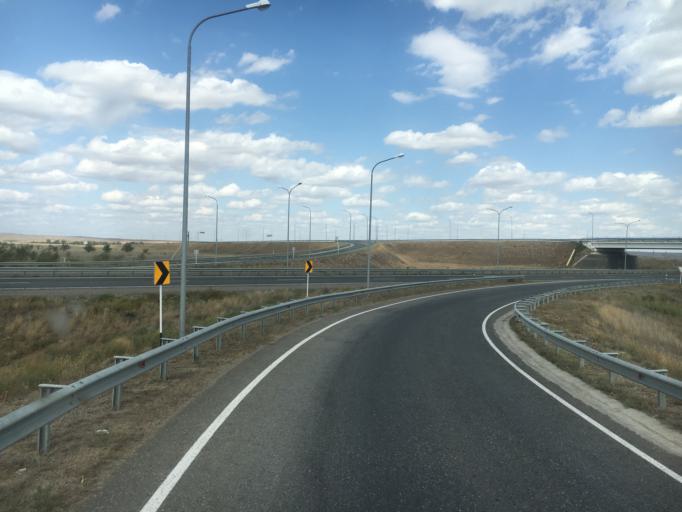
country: KZ
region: Aqtoebe
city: Aqtobe
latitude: 50.2934
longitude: 57.4345
